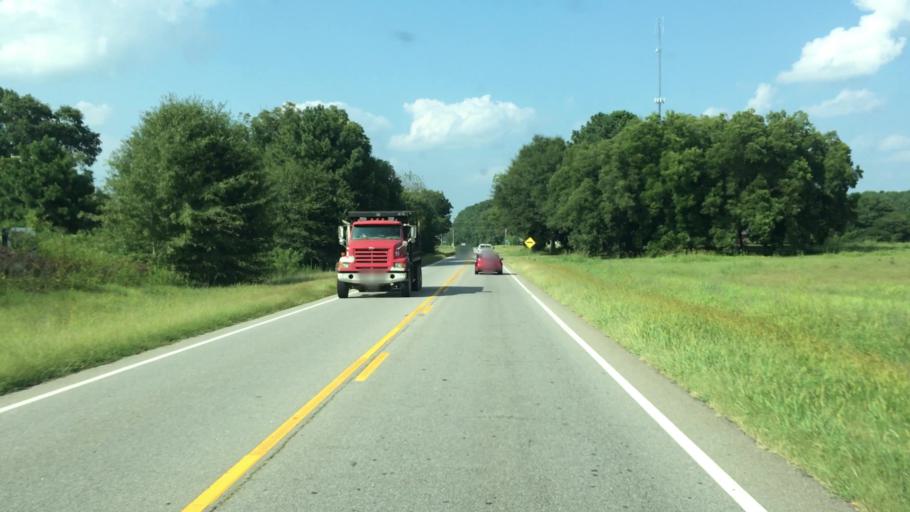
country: US
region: Georgia
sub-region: Walton County
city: Social Circle
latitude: 33.7083
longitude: -83.7015
